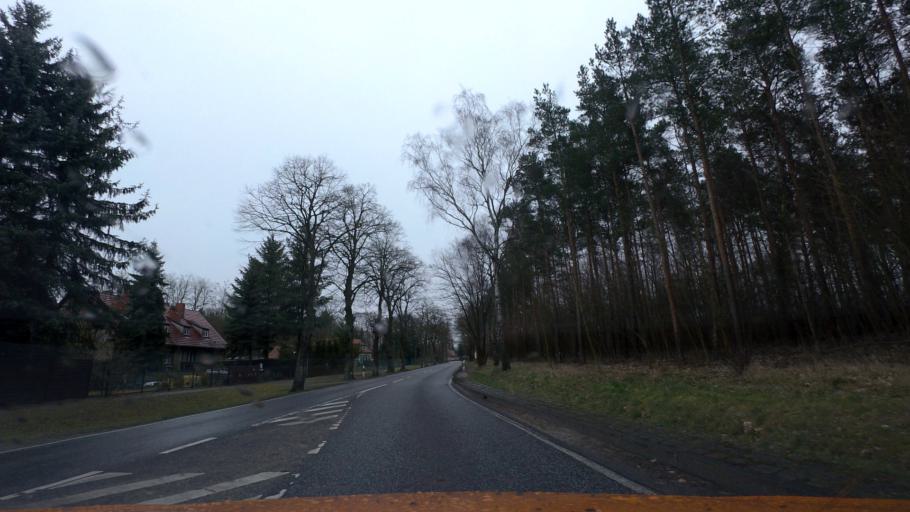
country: DE
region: Brandenburg
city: Falkensee
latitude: 52.6369
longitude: 13.0786
